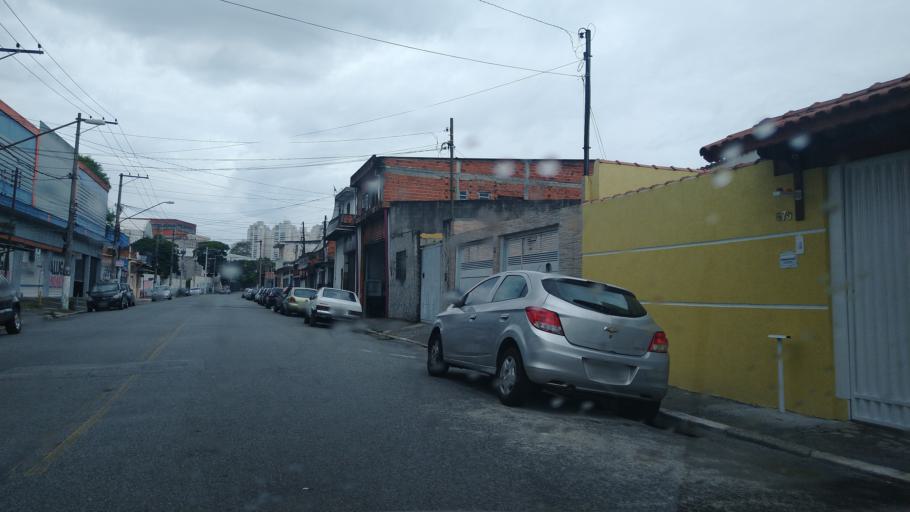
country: BR
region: Sao Paulo
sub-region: Guarulhos
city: Guarulhos
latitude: -23.4768
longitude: -46.5348
